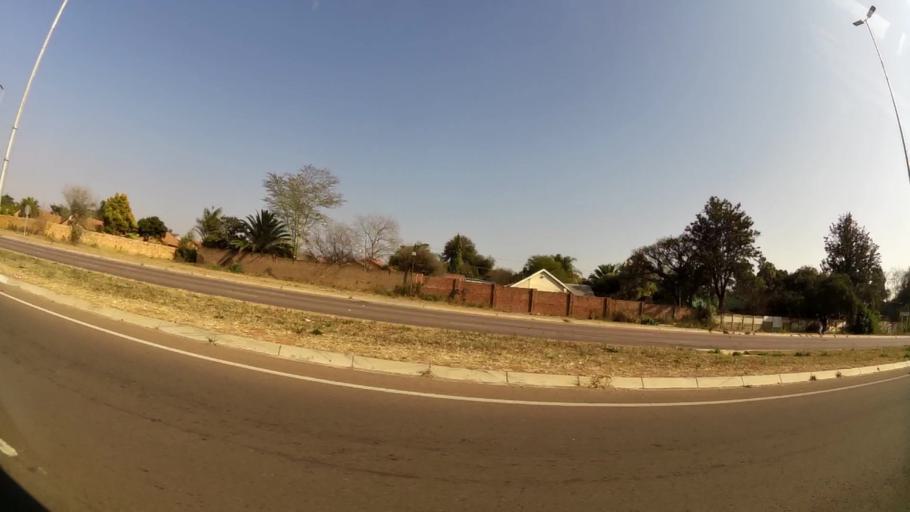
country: ZA
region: Gauteng
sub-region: City of Tshwane Metropolitan Municipality
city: Pretoria
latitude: -25.7429
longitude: 28.3284
